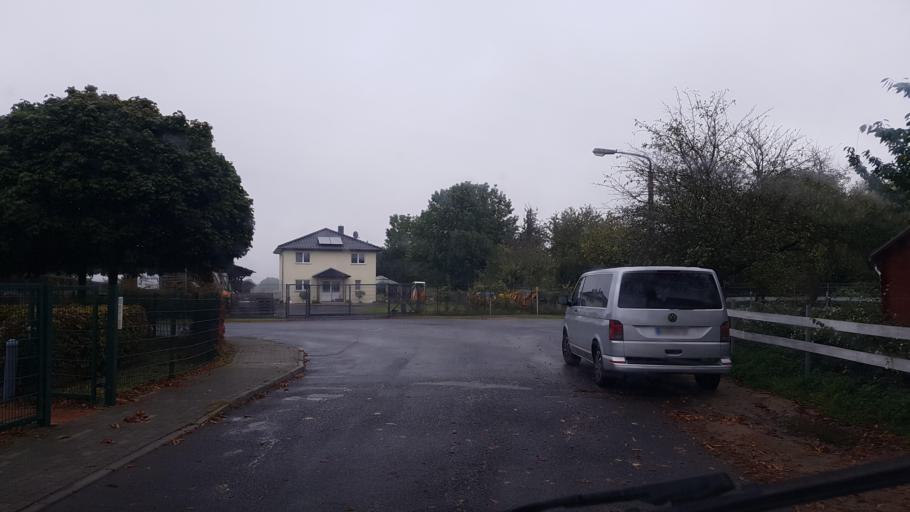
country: DE
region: Brandenburg
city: Furstenwalde
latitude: 52.4020
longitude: 14.0679
